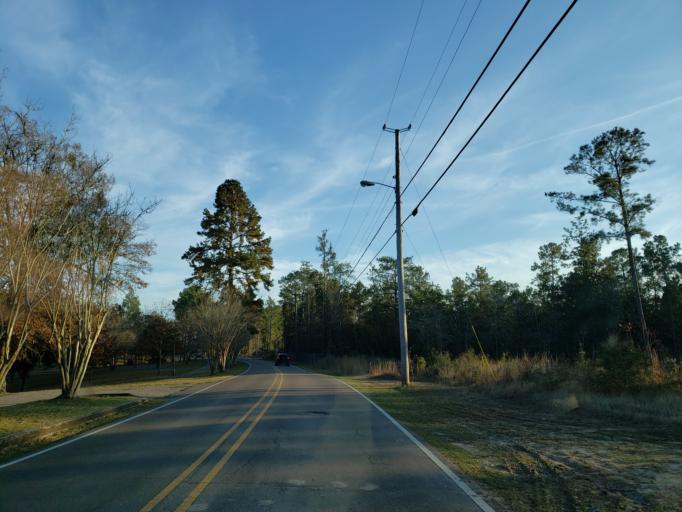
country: US
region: Mississippi
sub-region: Lamar County
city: Arnold Line
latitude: 31.3411
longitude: -89.3448
